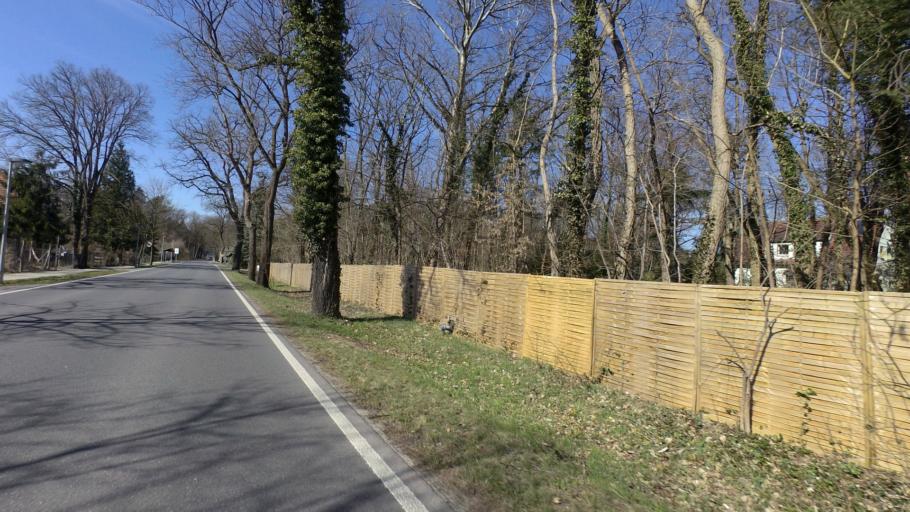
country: DE
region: Brandenburg
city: Waldsieversdorf
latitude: 52.5409
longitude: 14.0554
